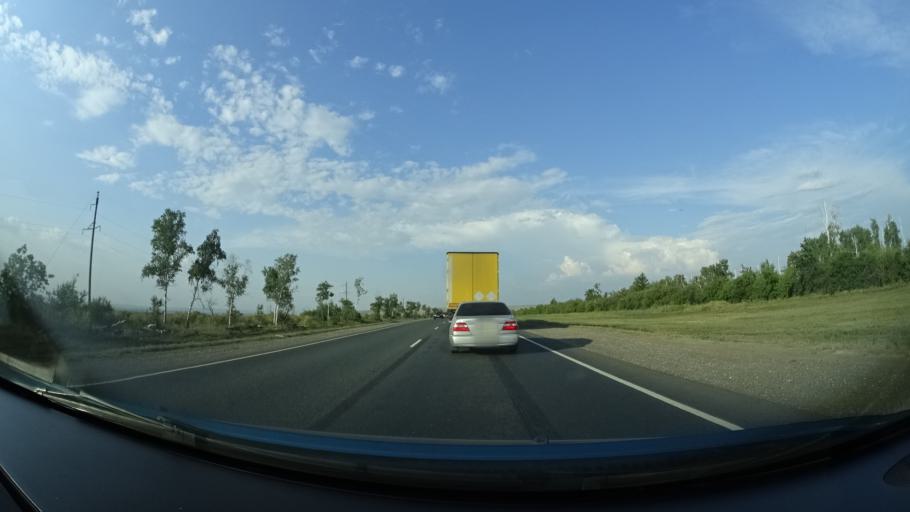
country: RU
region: Samara
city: Krasnyy Yar
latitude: 53.6725
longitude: 50.7687
